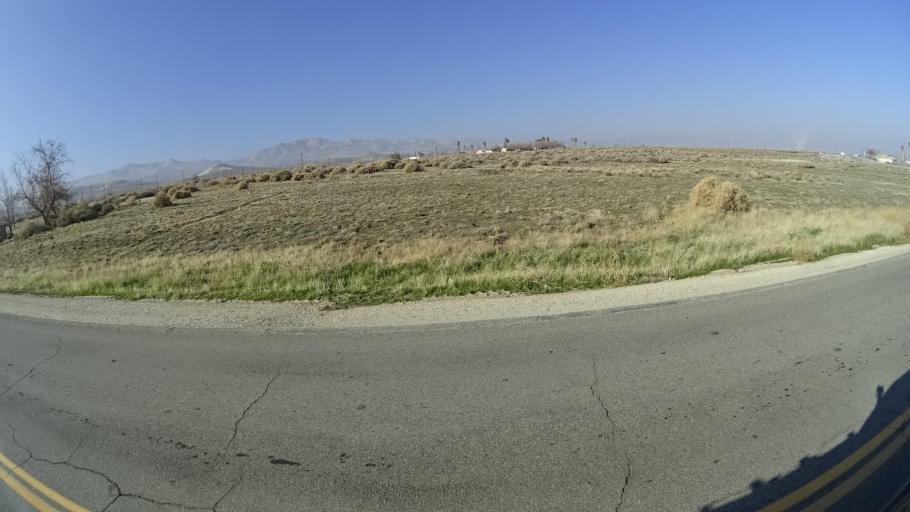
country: US
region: California
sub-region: Kern County
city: Taft Heights
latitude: 35.1820
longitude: -119.5503
